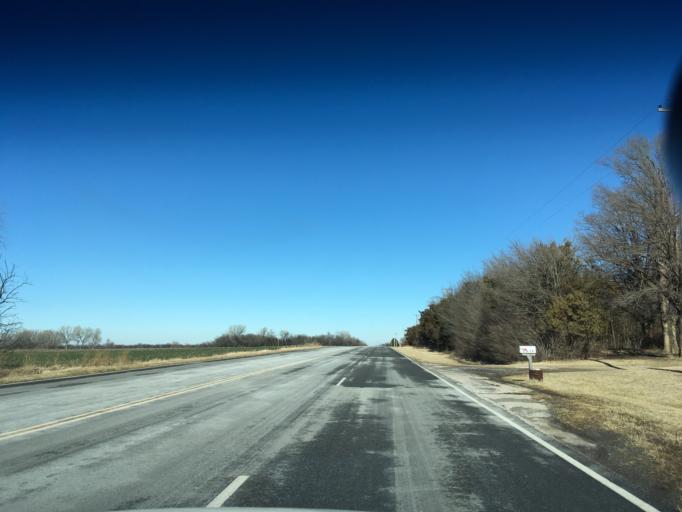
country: US
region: Kansas
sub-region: Harvey County
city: Sedgwick
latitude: 37.9227
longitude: -97.3364
